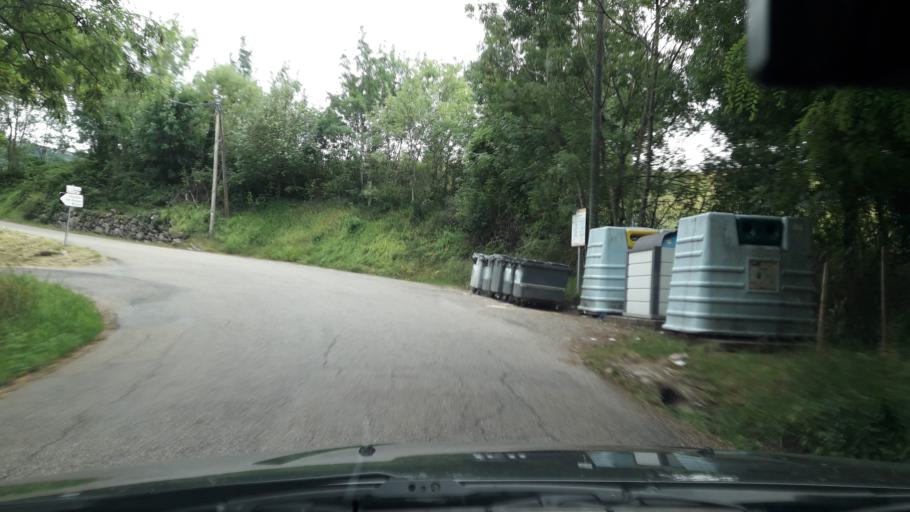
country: FR
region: Rhone-Alpes
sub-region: Departement de l'Ardeche
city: Alissas
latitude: 44.6875
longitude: 4.6319
